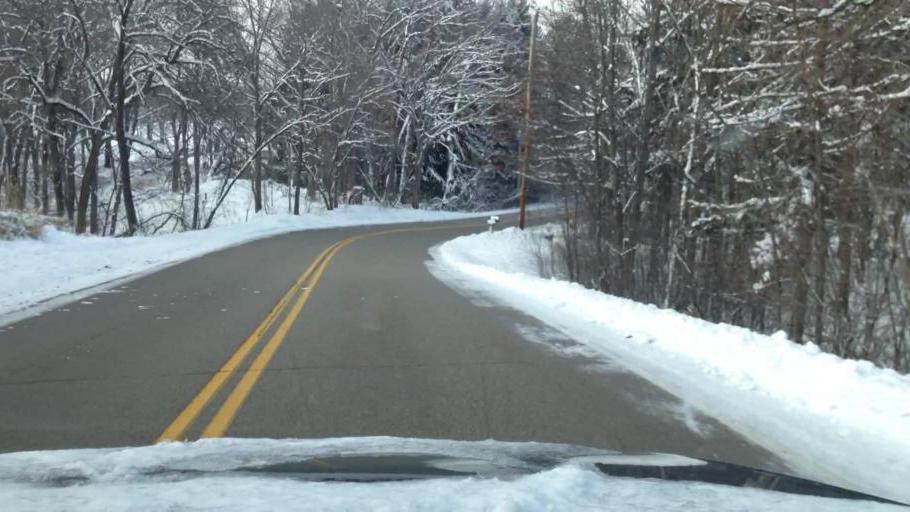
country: US
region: Wisconsin
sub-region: Waukesha County
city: Eagle
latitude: 42.8457
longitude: -88.4280
